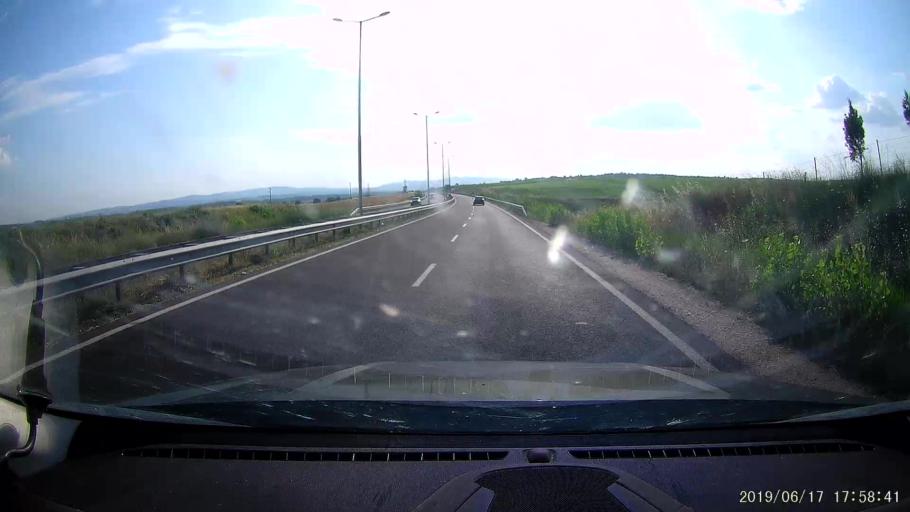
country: BG
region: Khaskovo
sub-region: Obshtina Svilengrad
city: Svilengrad
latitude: 41.7262
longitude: 26.3166
